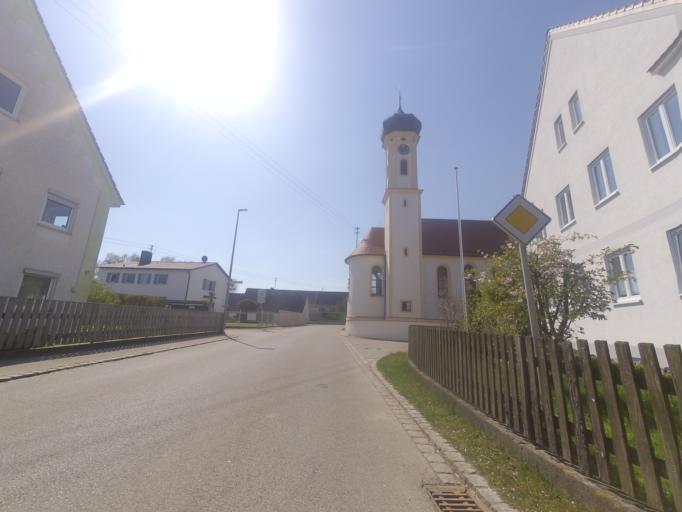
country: DE
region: Bavaria
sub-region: Swabia
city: Pfaffenhofen an der Roth
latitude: 48.3443
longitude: 10.1980
